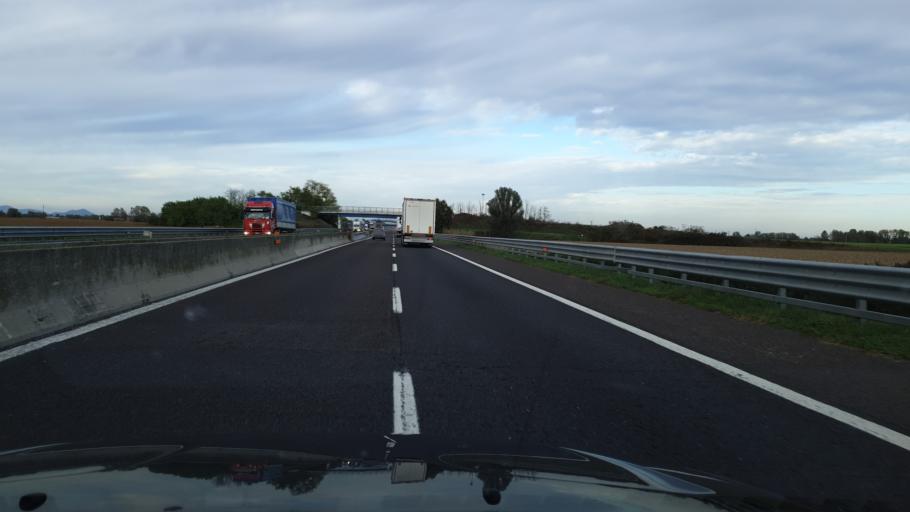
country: IT
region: Veneto
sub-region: Provincia di Rovigo
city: Costa di Rovigo
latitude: 45.0369
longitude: 11.7066
